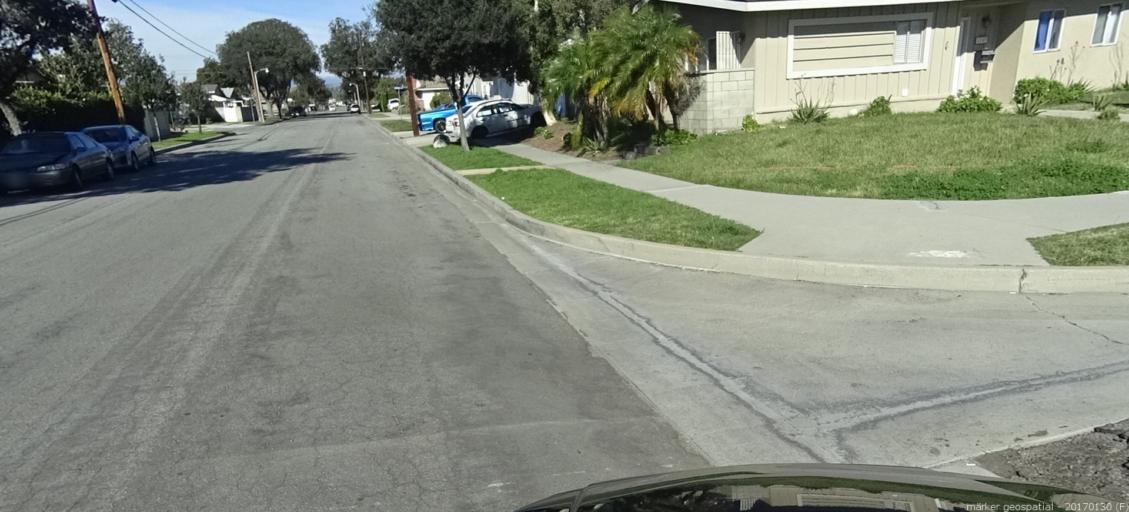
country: US
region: California
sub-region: Orange County
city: Fullerton
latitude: 33.8554
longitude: -117.9498
